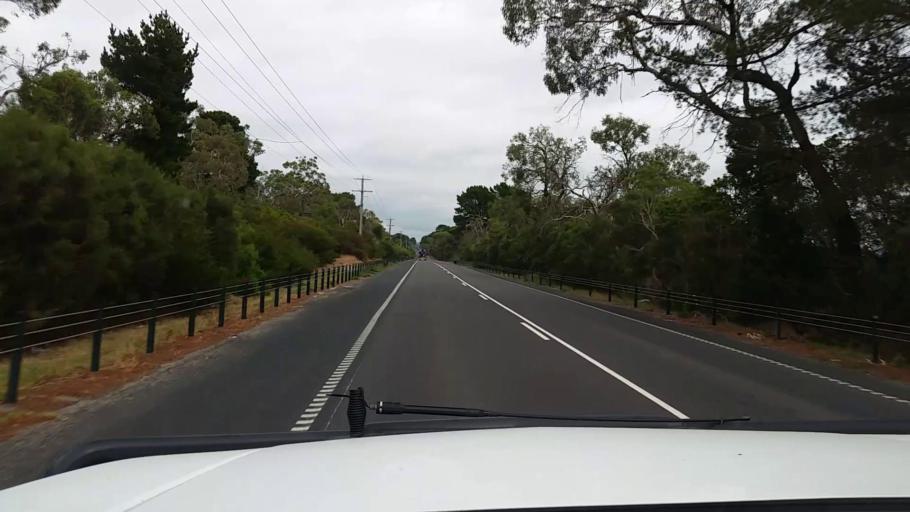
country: AU
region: Victoria
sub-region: Mornington Peninsula
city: Tyabb
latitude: -38.2545
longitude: 145.2131
